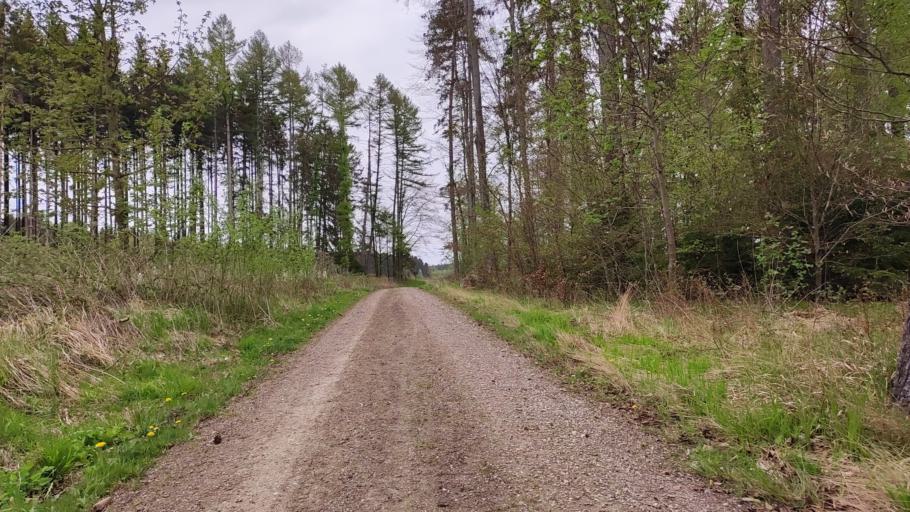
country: DE
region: Bavaria
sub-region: Swabia
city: Holzheim
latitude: 48.4909
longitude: 10.5476
